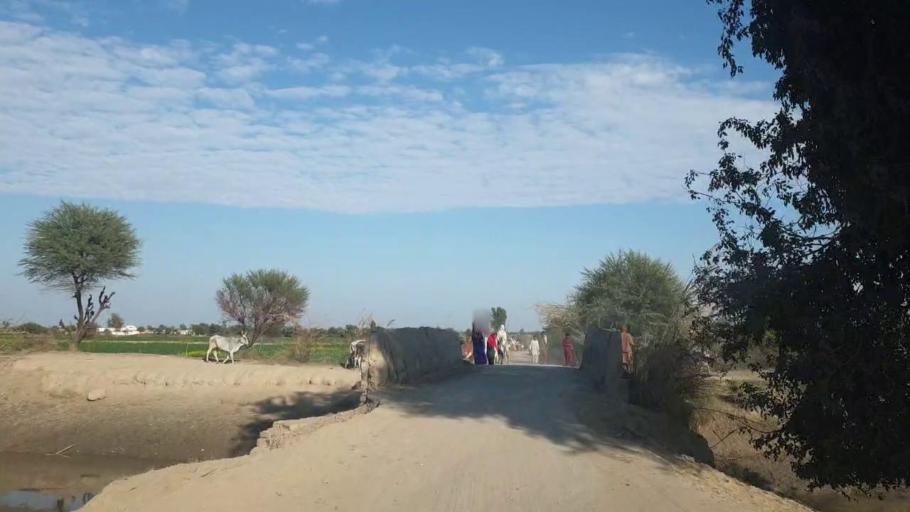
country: PK
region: Sindh
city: Sinjhoro
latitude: 26.0750
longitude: 68.8709
